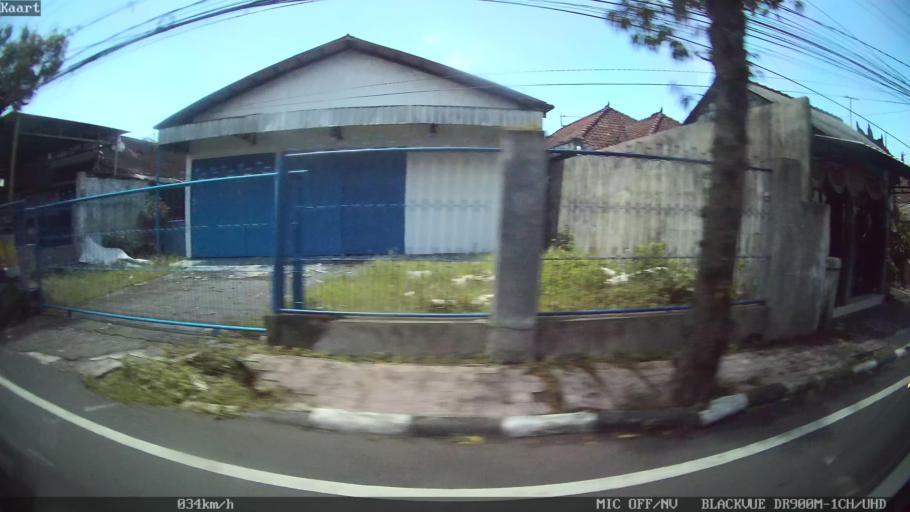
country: ID
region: Bali
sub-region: Kabupaten Gianyar
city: Ubud
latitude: -8.5556
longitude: 115.3025
